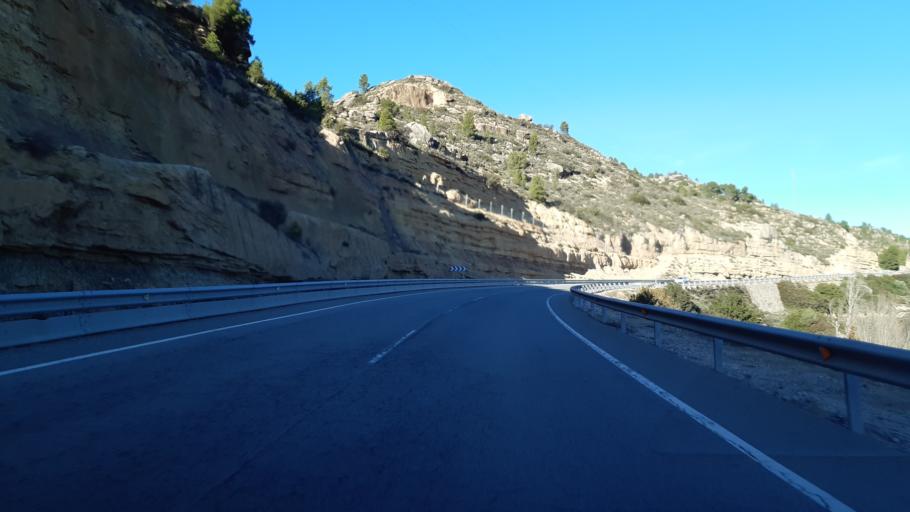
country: ES
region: Catalonia
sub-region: Provincia de Tarragona
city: Caseres
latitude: 41.0401
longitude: 0.2422
